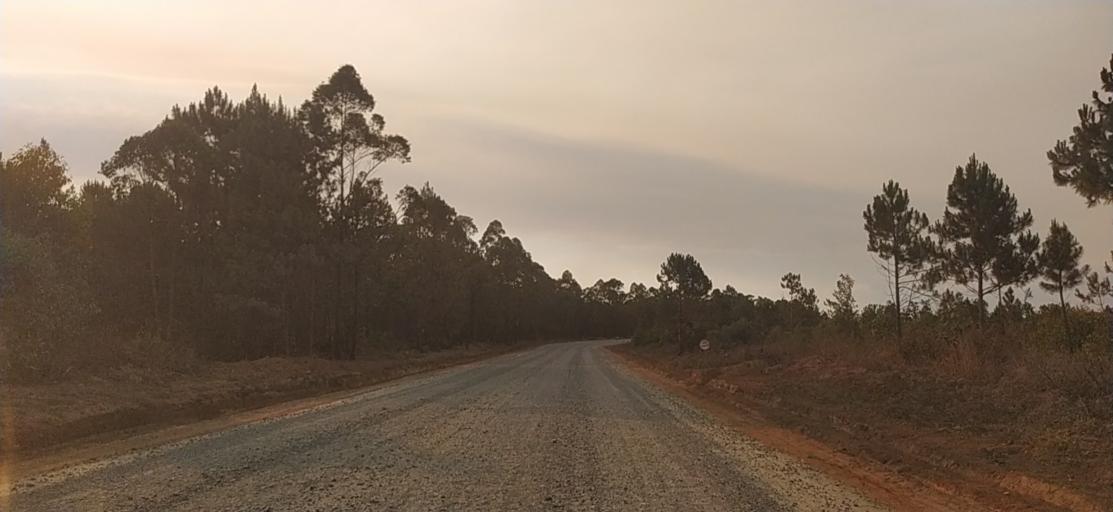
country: MG
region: Alaotra Mangoro
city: Moramanga
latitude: -18.5611
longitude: 48.2610
